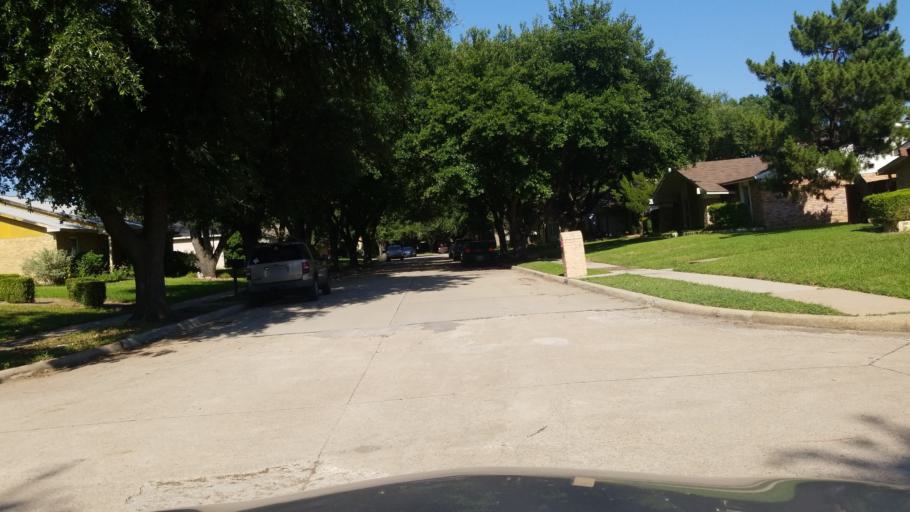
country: US
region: Texas
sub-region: Dallas County
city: Grand Prairie
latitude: 32.6842
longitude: -97.0155
